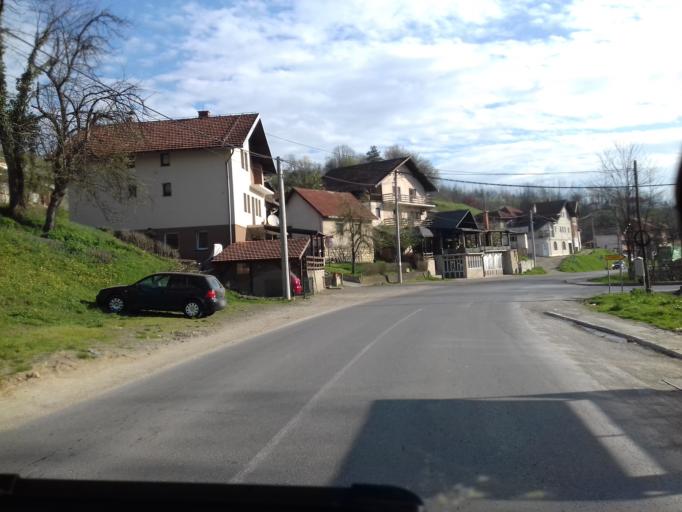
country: BA
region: Federation of Bosnia and Herzegovina
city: Tesanjka
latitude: 44.6379
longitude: 18.0133
